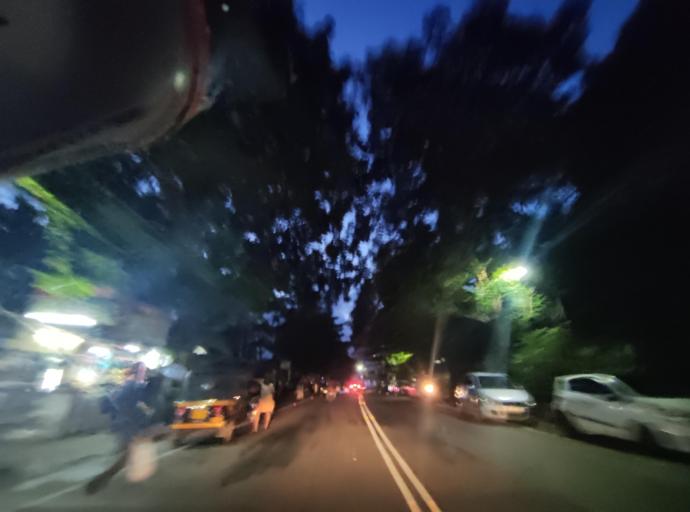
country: IN
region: Kerala
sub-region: Thiruvananthapuram
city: Thiruvananthapuram
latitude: 8.5392
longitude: 76.9634
